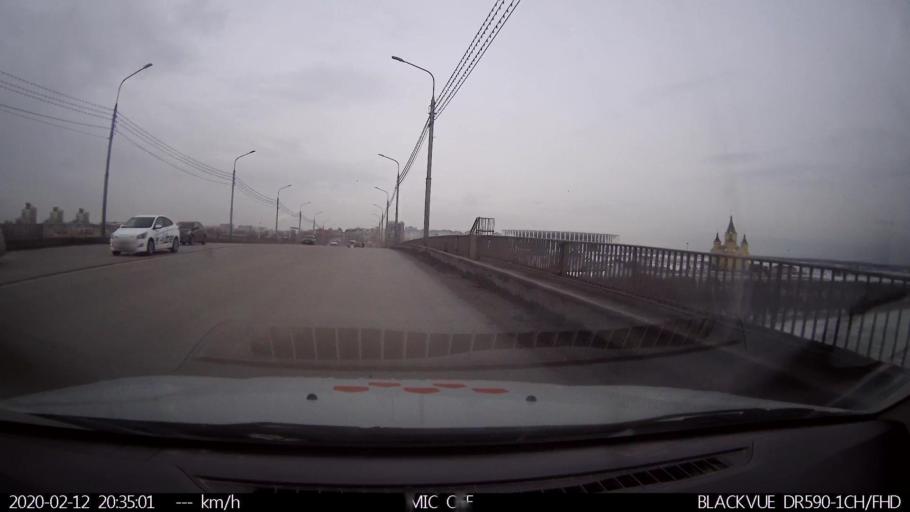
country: RU
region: Nizjnij Novgorod
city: Nizhniy Novgorod
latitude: 56.3304
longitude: 43.9739
